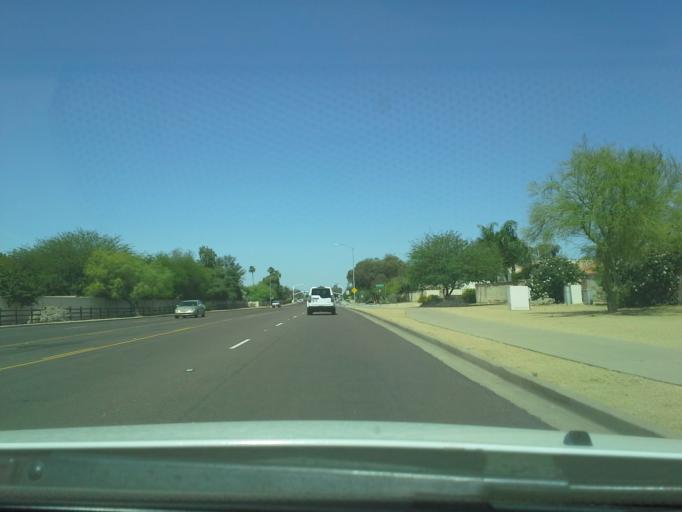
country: US
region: Arizona
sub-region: Maricopa County
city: Paradise Valley
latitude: 33.5968
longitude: -111.9214
